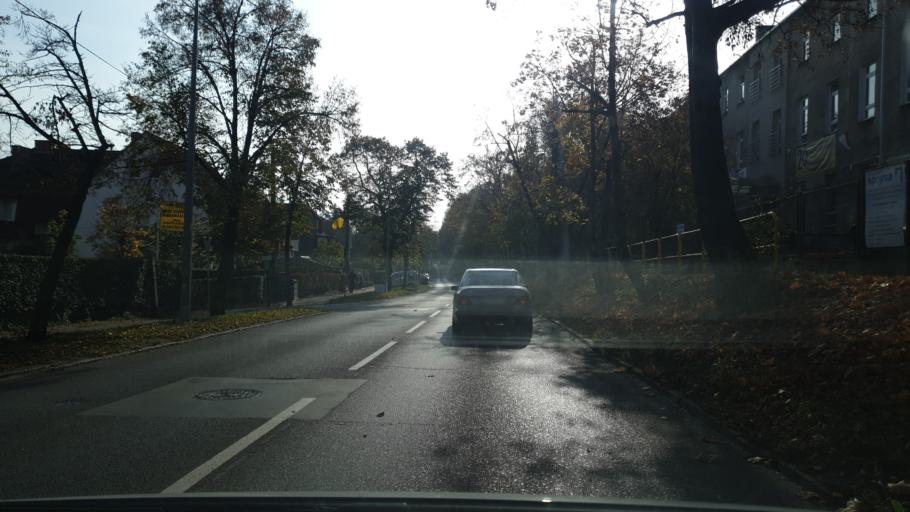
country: PL
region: Pomeranian Voivodeship
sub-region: Sopot
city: Sopot
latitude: 54.4028
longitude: 18.5610
